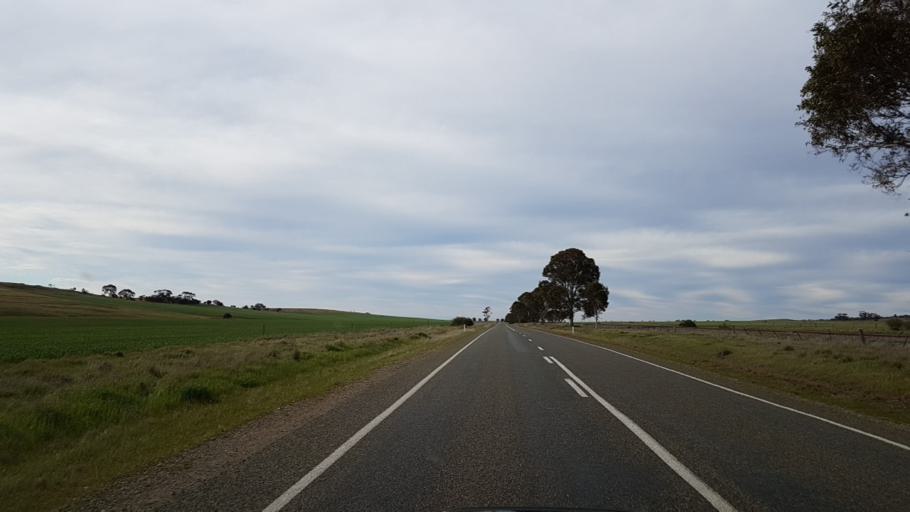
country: AU
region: South Australia
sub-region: Northern Areas
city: Jamestown
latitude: -33.1307
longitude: 138.6178
